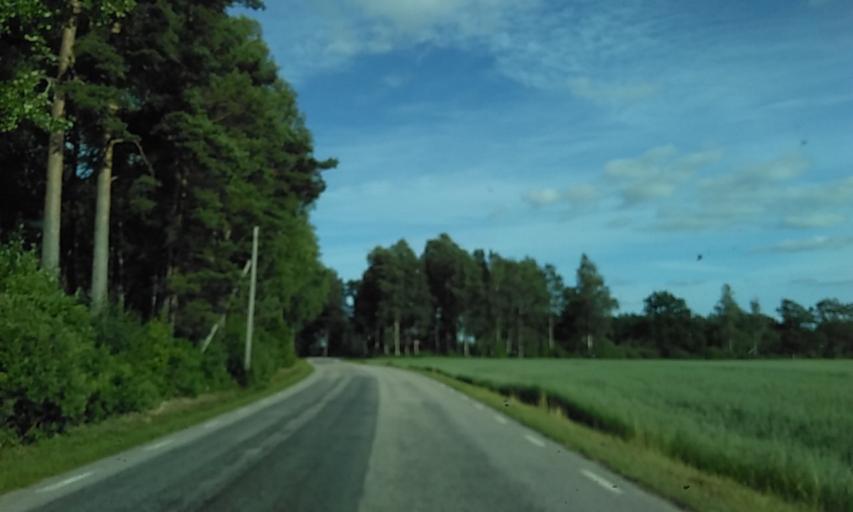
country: SE
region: Vaestra Goetaland
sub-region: Vara Kommun
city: Vara
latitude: 58.3481
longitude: 12.8861
